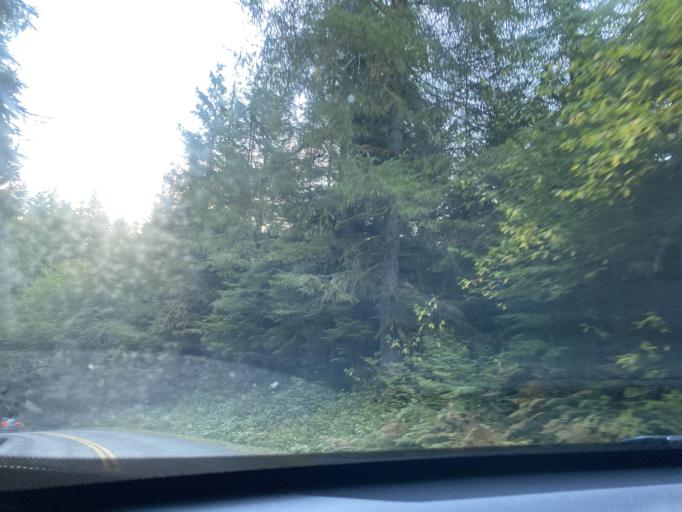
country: US
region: Washington
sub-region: Clallam County
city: Forks
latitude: 47.8091
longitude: -124.1020
